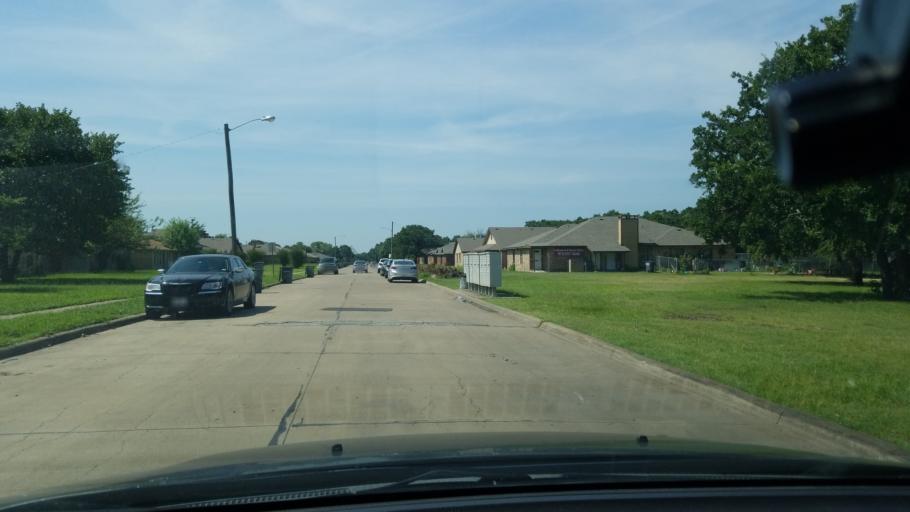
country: US
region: Texas
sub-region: Dallas County
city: Balch Springs
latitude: 32.7334
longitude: -96.6351
